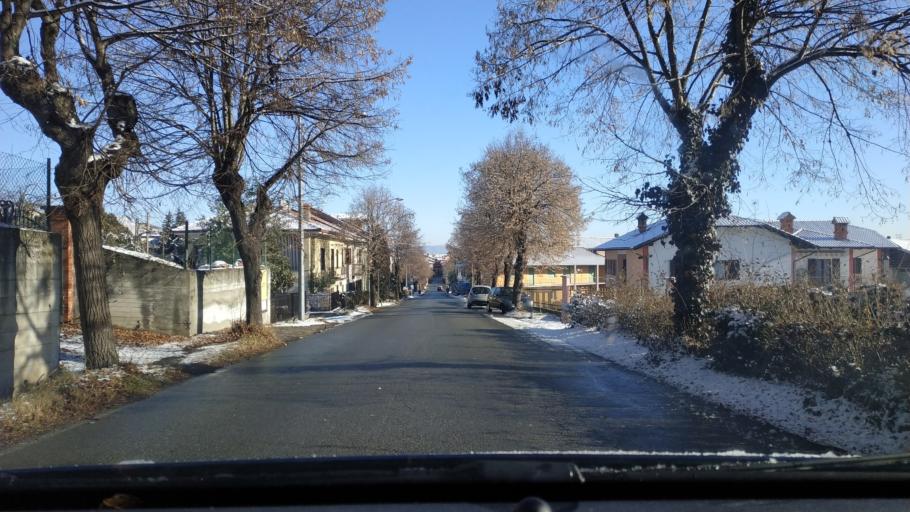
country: IT
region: Piedmont
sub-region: Provincia di Torino
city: Candia Canavese
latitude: 45.3260
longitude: 7.8826
